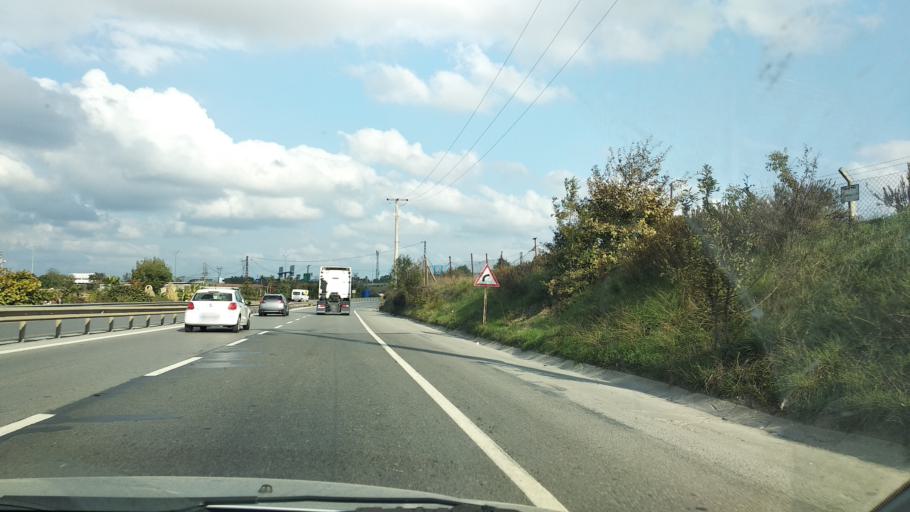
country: TR
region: Istanbul
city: Sultanbeyli
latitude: 40.9313
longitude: 29.3372
